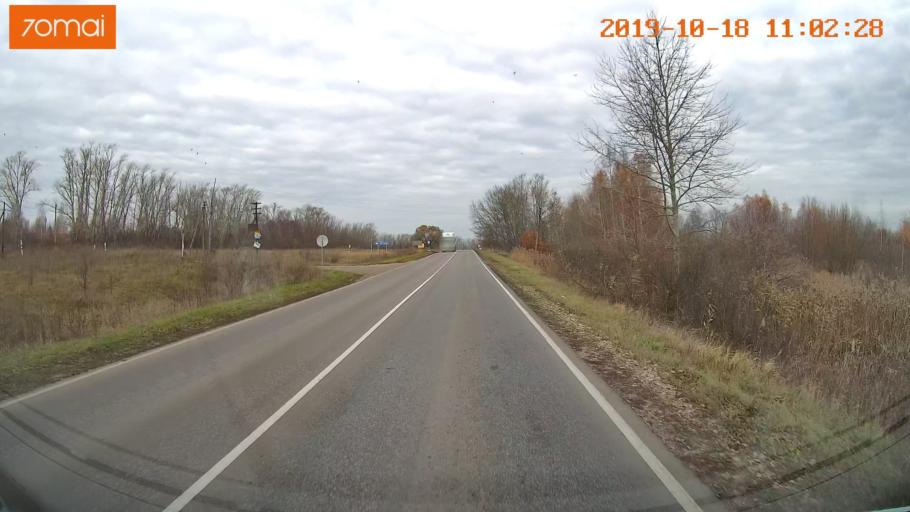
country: RU
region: Tula
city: Yepifan'
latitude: 53.8660
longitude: 38.5445
